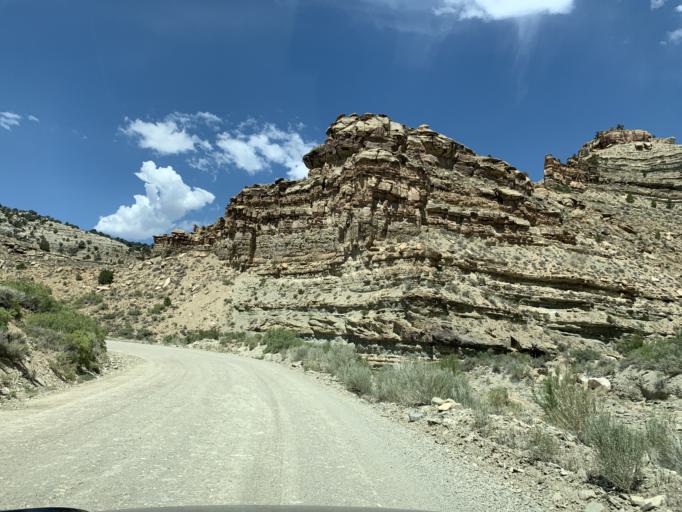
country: US
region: Utah
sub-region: Carbon County
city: East Carbon City
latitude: 39.8310
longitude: -110.2474
